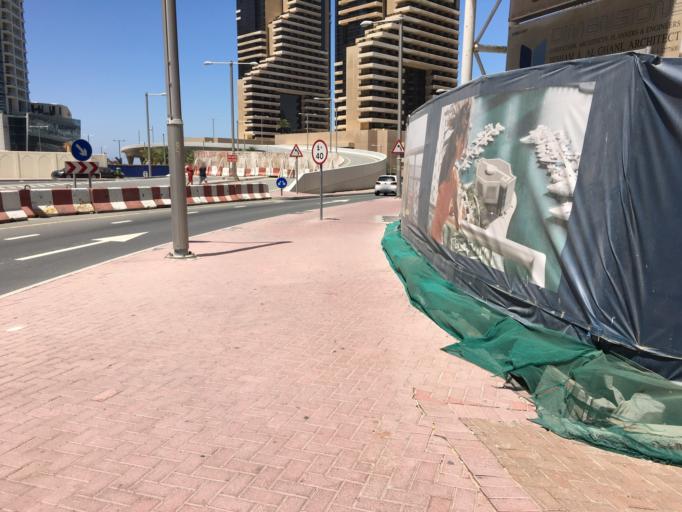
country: AE
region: Dubai
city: Dubai
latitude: 25.0838
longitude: 55.1436
